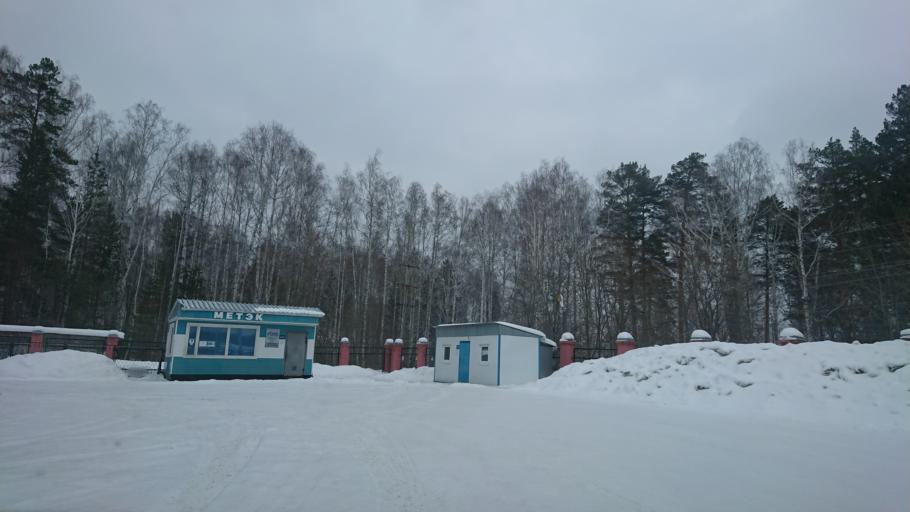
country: RU
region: Sverdlovsk
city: Sysert'
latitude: 56.4474
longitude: 60.8917
